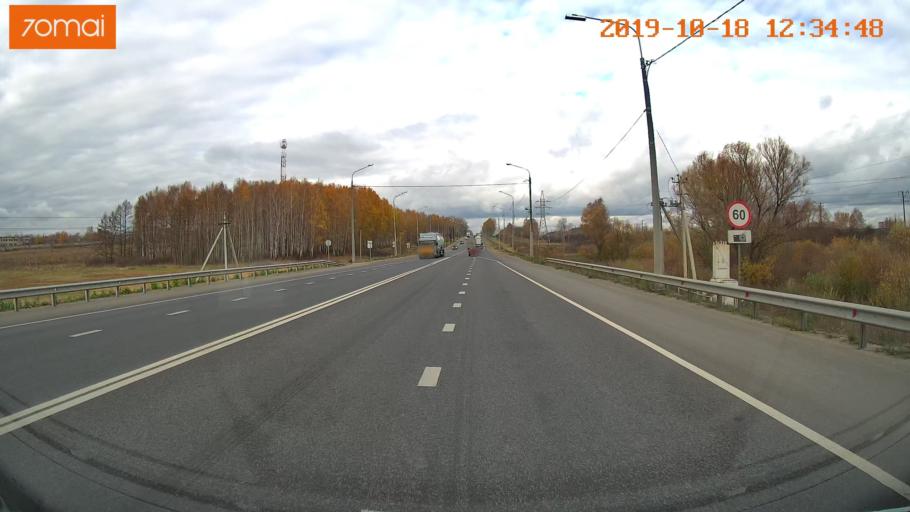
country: RU
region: Rjazan
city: Ryazan'
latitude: 54.6179
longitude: 39.6368
